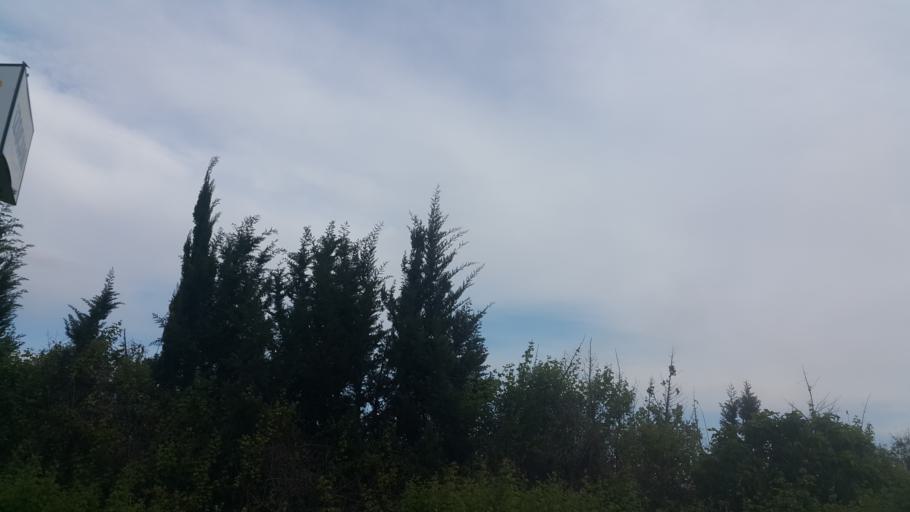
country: TR
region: Mersin
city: Yenice
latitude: 36.9430
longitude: 34.9781
